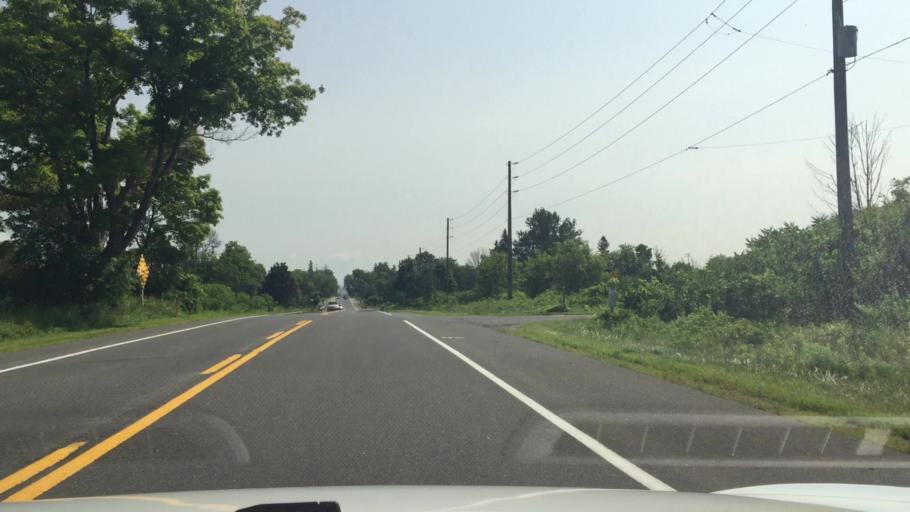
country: CA
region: Ontario
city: Pickering
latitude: 43.9163
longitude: -79.1167
